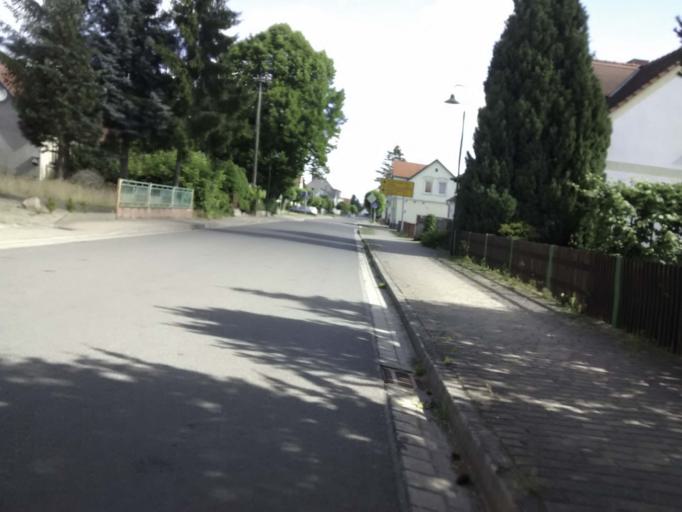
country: DE
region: Saxony-Anhalt
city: Jerichow
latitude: 52.4128
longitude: 11.9640
